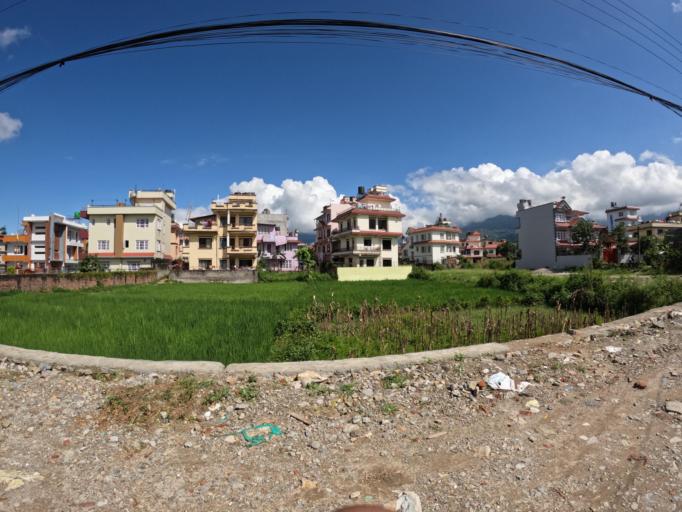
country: NP
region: Central Region
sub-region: Bagmati Zone
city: Kathmandu
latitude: 27.7502
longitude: 85.3348
